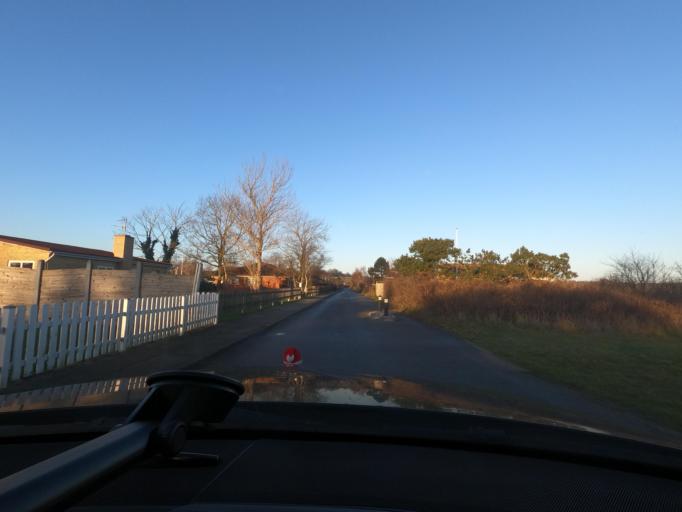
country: DK
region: South Denmark
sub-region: Sonderborg Kommune
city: Broager
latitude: 54.8982
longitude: 9.7015
